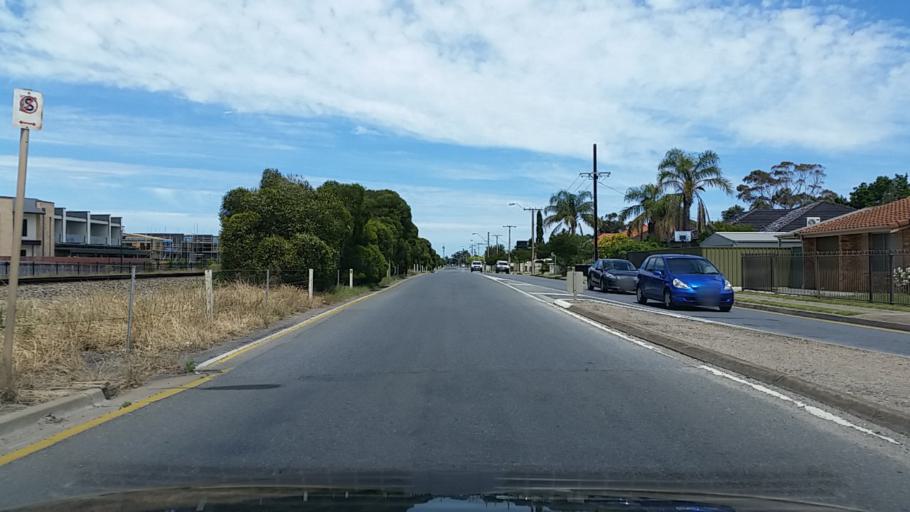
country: AU
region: South Australia
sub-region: Charles Sturt
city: Woodville West
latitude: -34.8841
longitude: 138.5207
